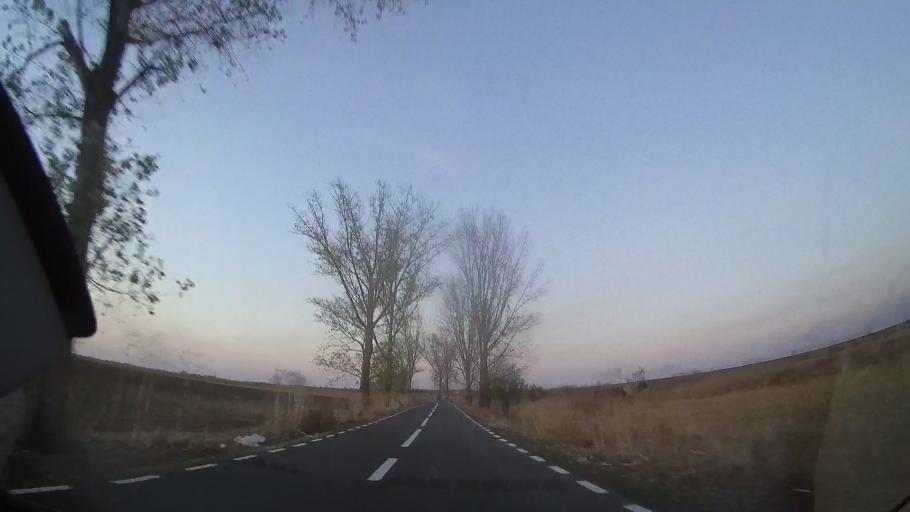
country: RO
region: Constanta
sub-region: Comuna Cobadin
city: Cobadin
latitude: 44.0386
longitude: 28.2579
